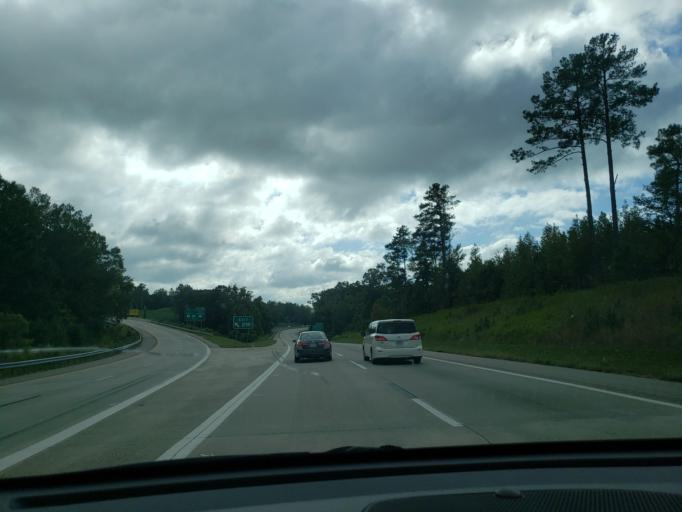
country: US
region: North Carolina
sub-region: Vance County
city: Henderson
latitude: 36.3719
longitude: -78.3606
